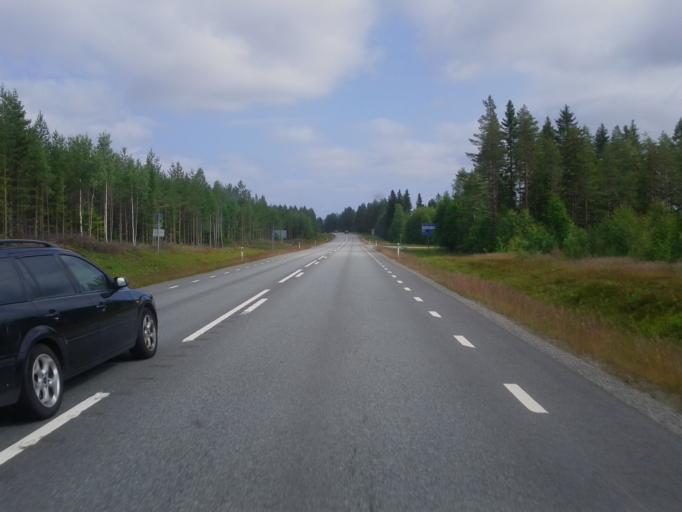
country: SE
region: Vaesterbotten
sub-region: Skelleftea Kommun
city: Burea
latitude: 64.3455
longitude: 21.2867
